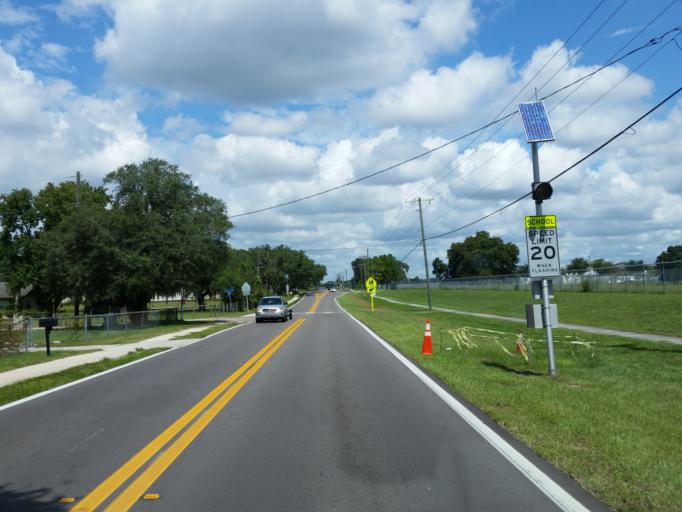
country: US
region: Florida
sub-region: Hillsborough County
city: Riverview
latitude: 27.8467
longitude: -82.3145
